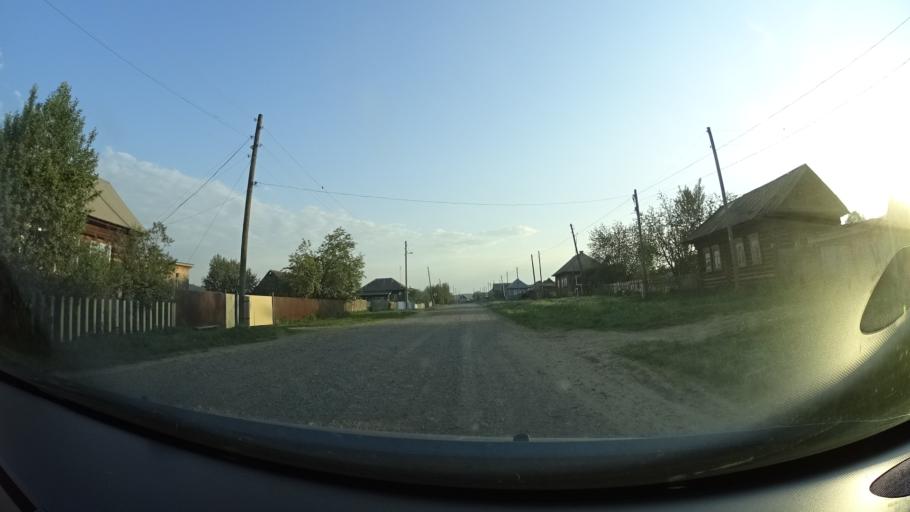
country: RU
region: Perm
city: Kuyeda
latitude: 56.6676
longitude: 55.6935
